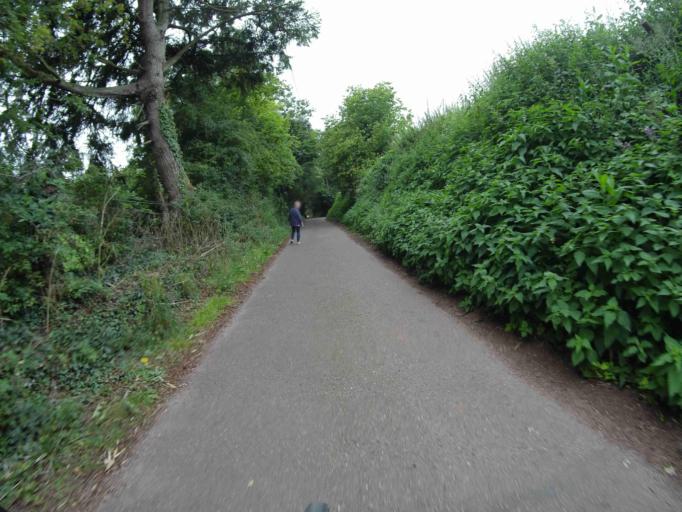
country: GB
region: England
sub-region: Devon
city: Heavitree
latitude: 50.7111
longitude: -3.4928
